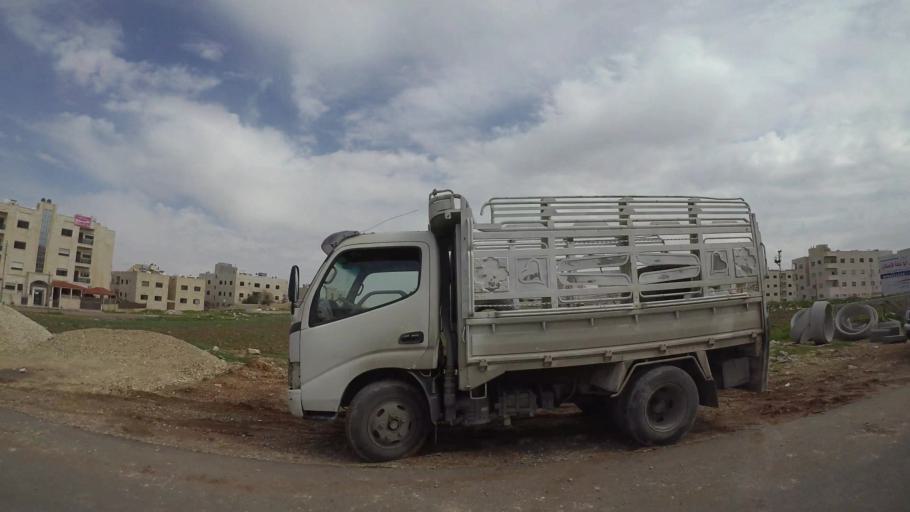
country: JO
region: Amman
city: Amman
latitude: 31.9946
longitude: 35.9341
